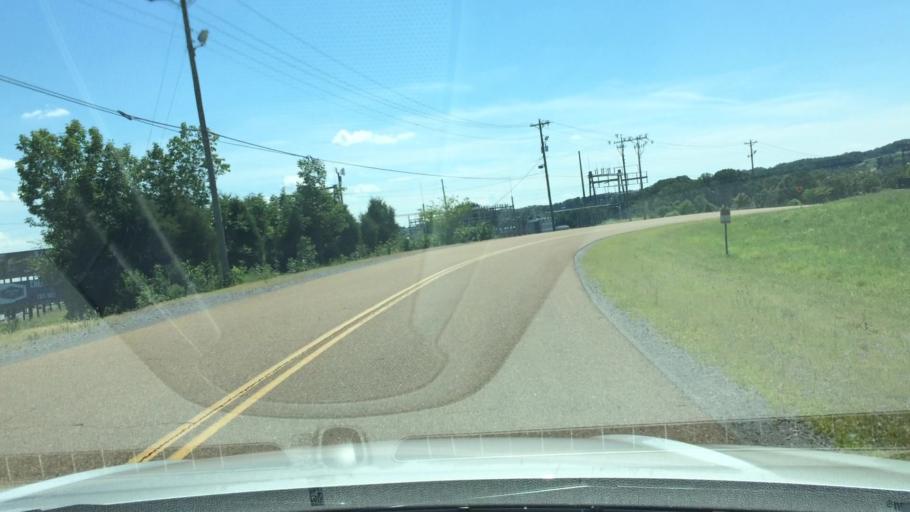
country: US
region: Tennessee
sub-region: McMinn County
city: Athens
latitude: 35.4712
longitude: -84.6449
